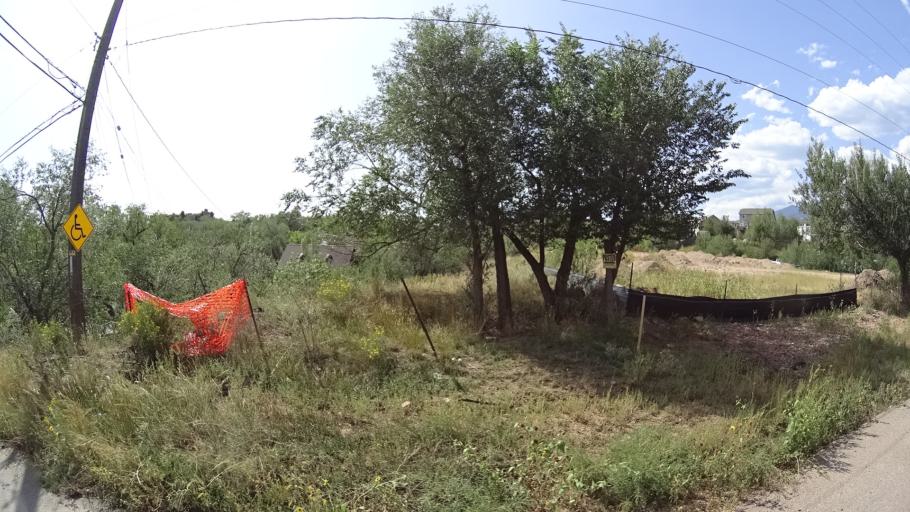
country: US
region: Colorado
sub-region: El Paso County
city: Colorado Springs
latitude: 38.8282
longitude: -104.8456
